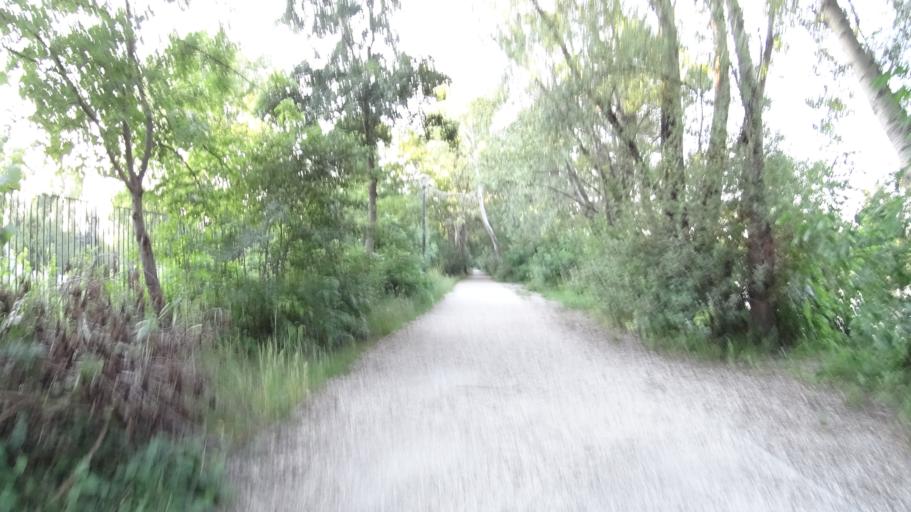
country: HU
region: Budapest
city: Budapest XXIII. keruelet
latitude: 47.4074
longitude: 19.1018
